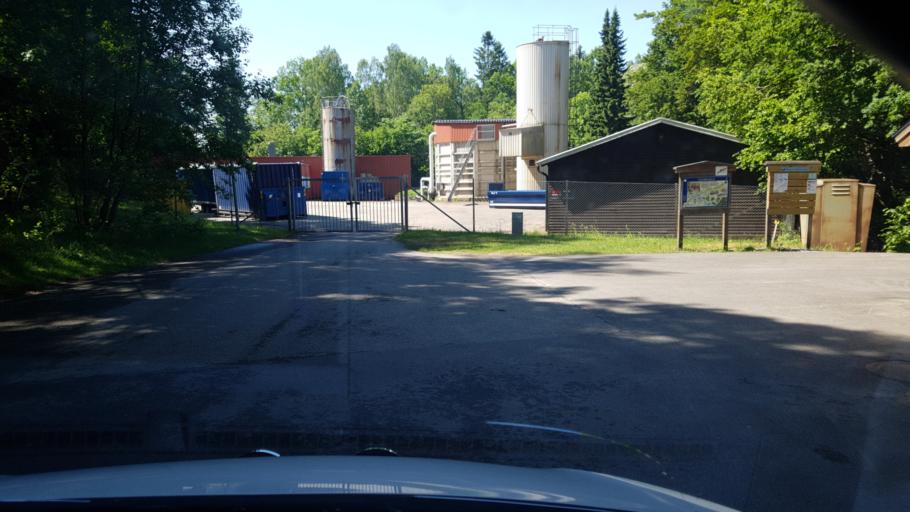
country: SE
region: Vaestra Goetaland
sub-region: Lerums Kommun
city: Stenkullen
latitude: 57.8039
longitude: 12.3524
